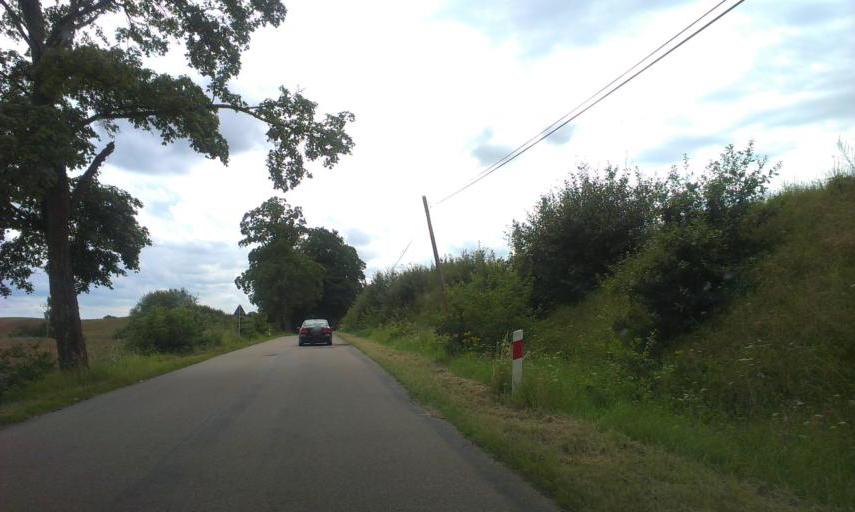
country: PL
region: West Pomeranian Voivodeship
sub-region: Powiat szczecinecki
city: Barwice
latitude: 53.7126
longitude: 16.3542
